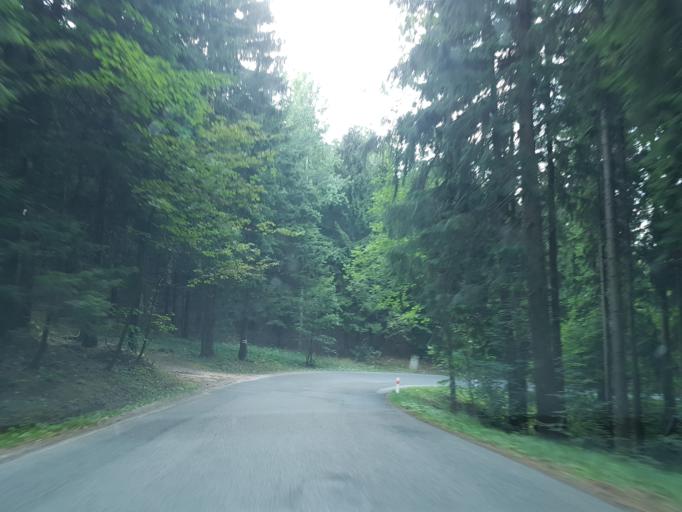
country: CZ
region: Liberecky
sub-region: Okres Jablonec nad Nisou
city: Jablonec nad Nisou
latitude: 50.7114
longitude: 15.1920
